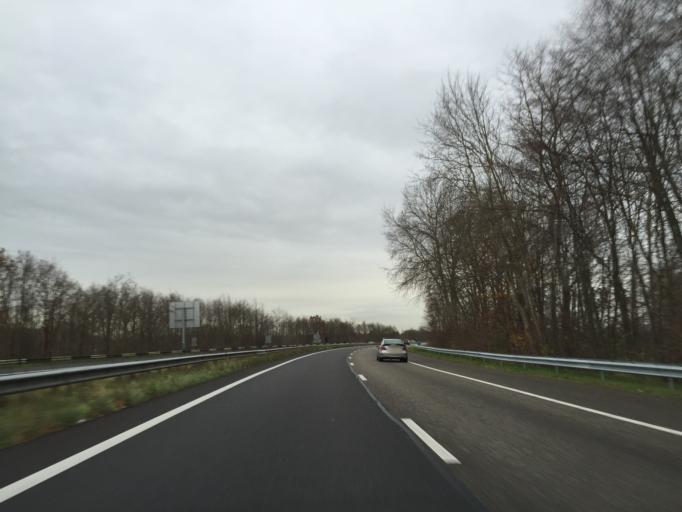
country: NL
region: North Brabant
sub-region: Gemeente Woensdrecht
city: Woensdrecht
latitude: 51.4454
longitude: 4.3151
